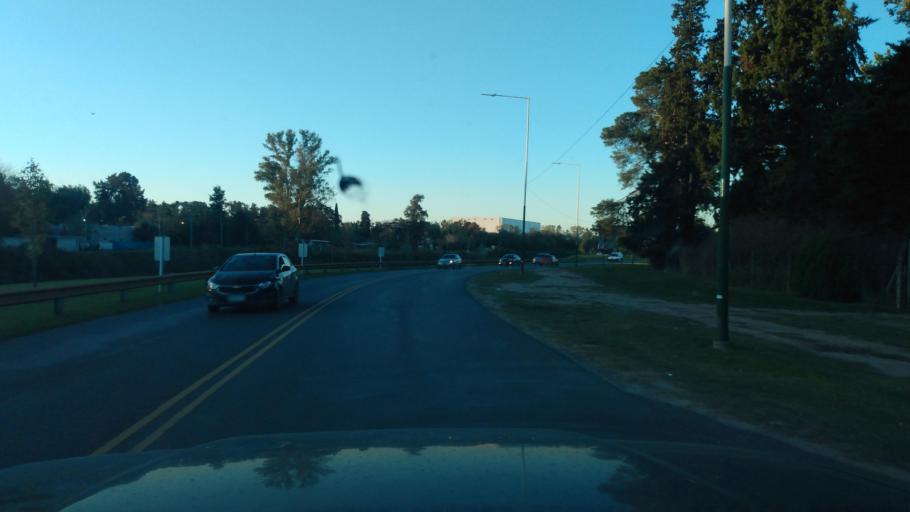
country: AR
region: Buenos Aires
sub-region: Partido de Merlo
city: Merlo
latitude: -34.6383
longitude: -58.7314
